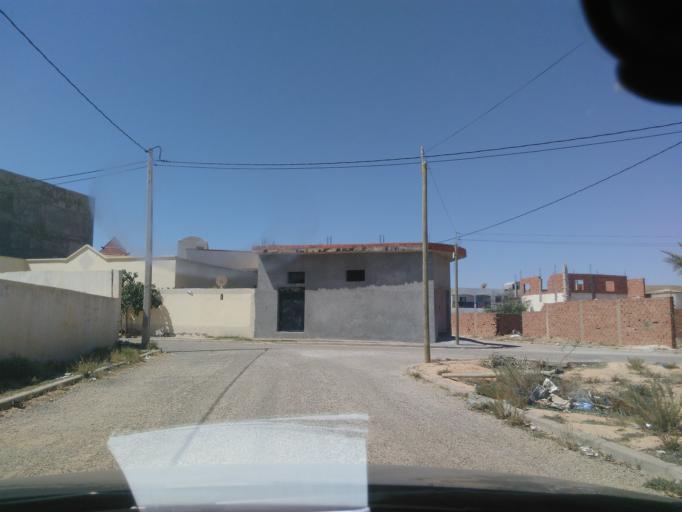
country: TN
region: Tataouine
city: Tataouine
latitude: 32.9509
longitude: 10.4703
